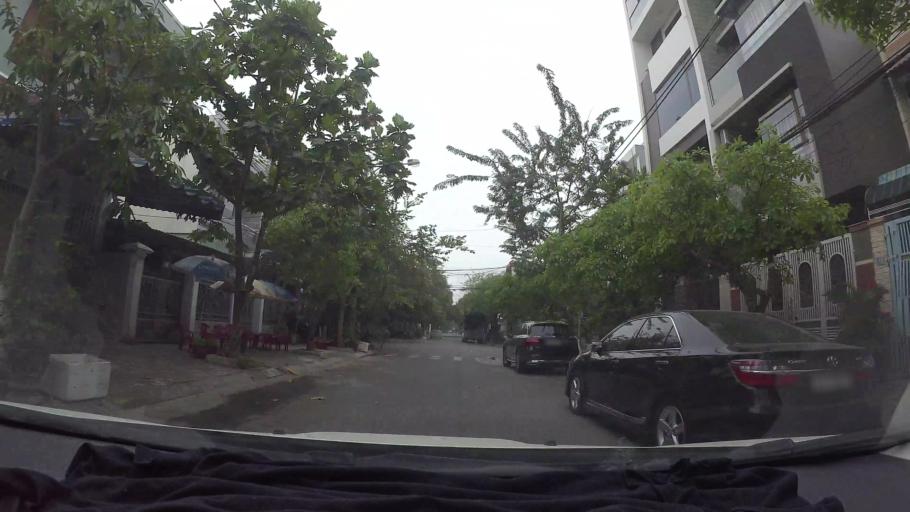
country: VN
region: Da Nang
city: Cam Le
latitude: 16.0268
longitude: 108.2122
